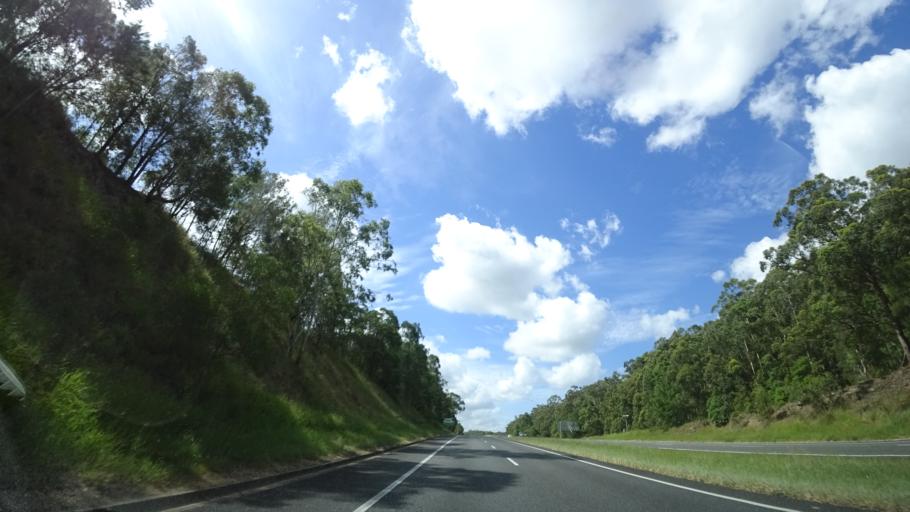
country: AU
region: Queensland
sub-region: Sunshine Coast
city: Nambour
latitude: -26.6026
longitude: 152.9726
